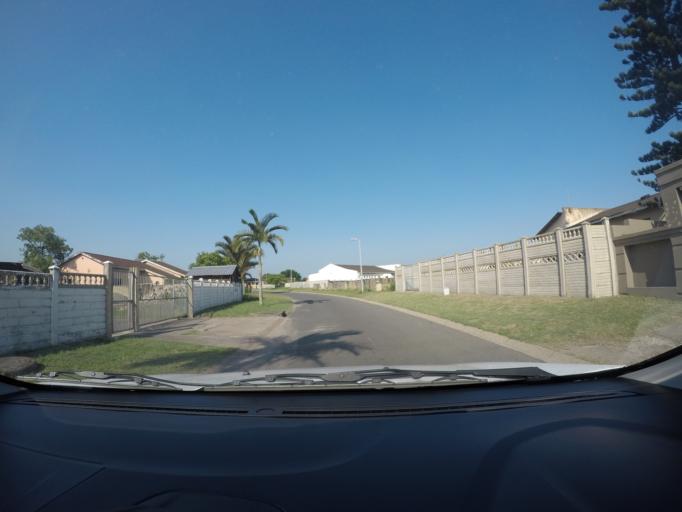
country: ZA
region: KwaZulu-Natal
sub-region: uThungulu District Municipality
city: Richards Bay
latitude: -28.7162
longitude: 32.0333
